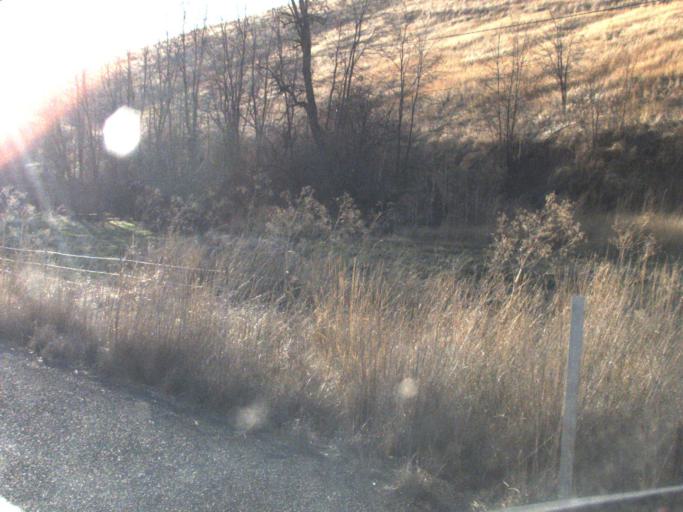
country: US
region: Washington
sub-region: Walla Walla County
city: Waitsburg
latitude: 46.1556
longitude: -118.1343
